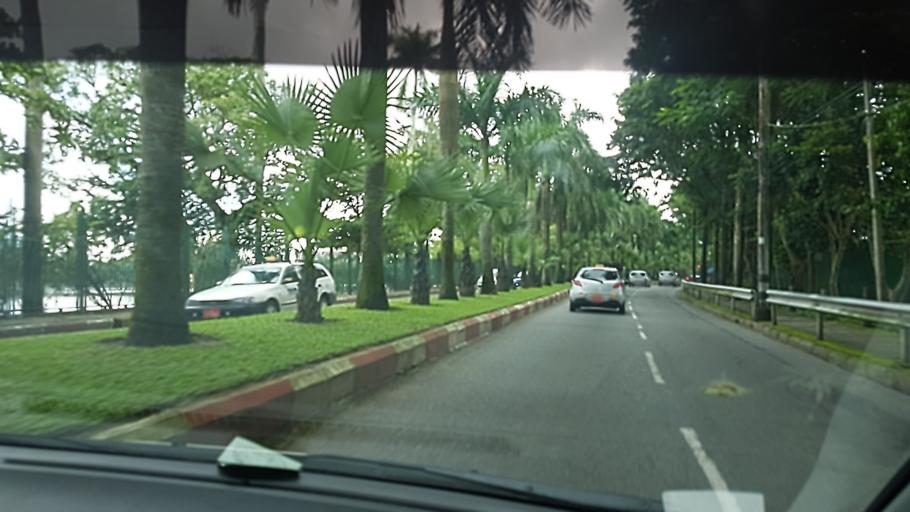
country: MM
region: Yangon
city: Yangon
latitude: 16.7935
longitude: 96.1639
